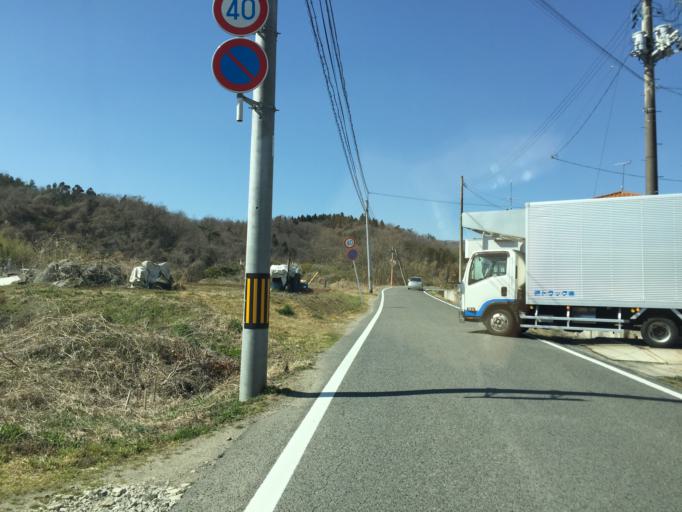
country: JP
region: Fukushima
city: Iwaki
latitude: 37.0604
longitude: 140.8454
